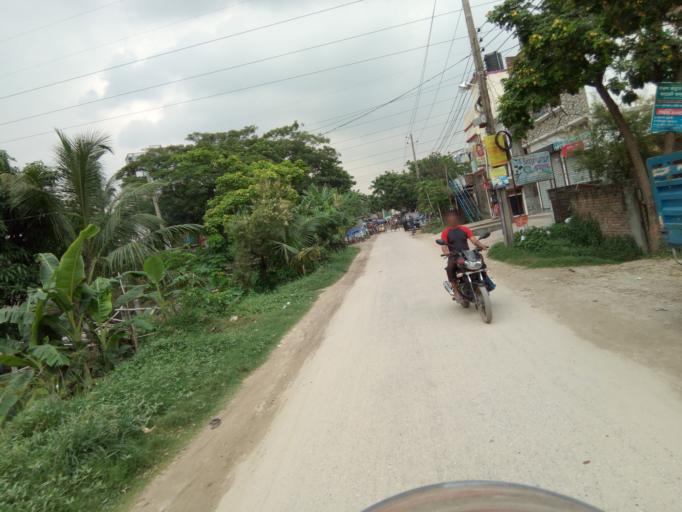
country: BD
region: Dhaka
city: Paltan
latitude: 23.7098
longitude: 90.4869
